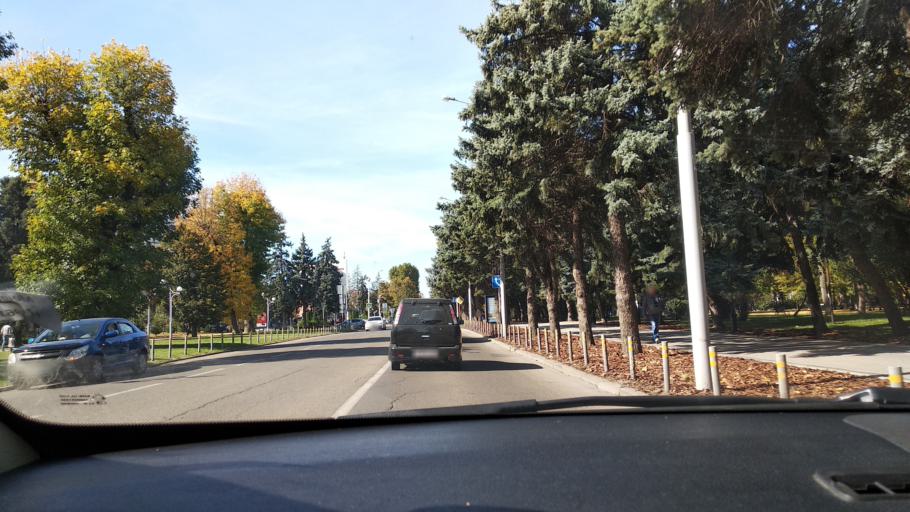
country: RU
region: Krasnodarskiy
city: Krasnodar
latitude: 45.0146
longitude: 38.9689
